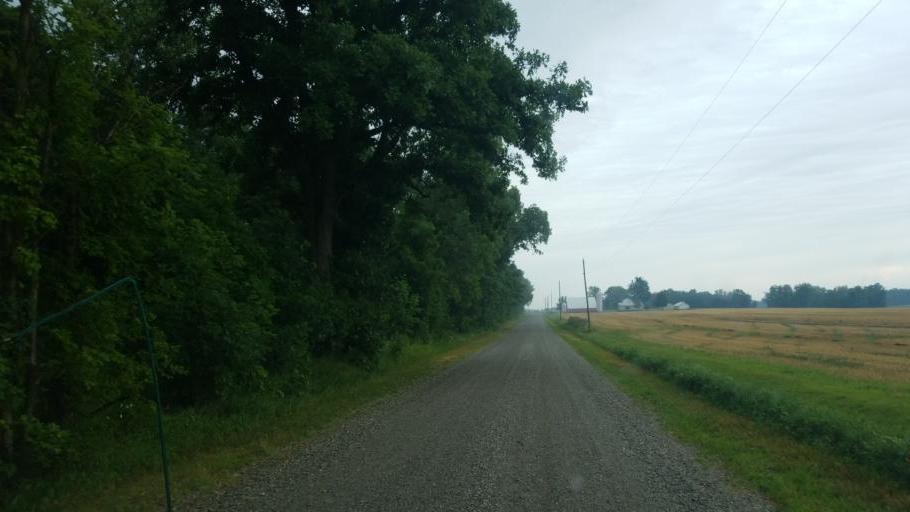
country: US
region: Indiana
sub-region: DeKalb County
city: Butler
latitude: 41.4548
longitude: -84.9099
